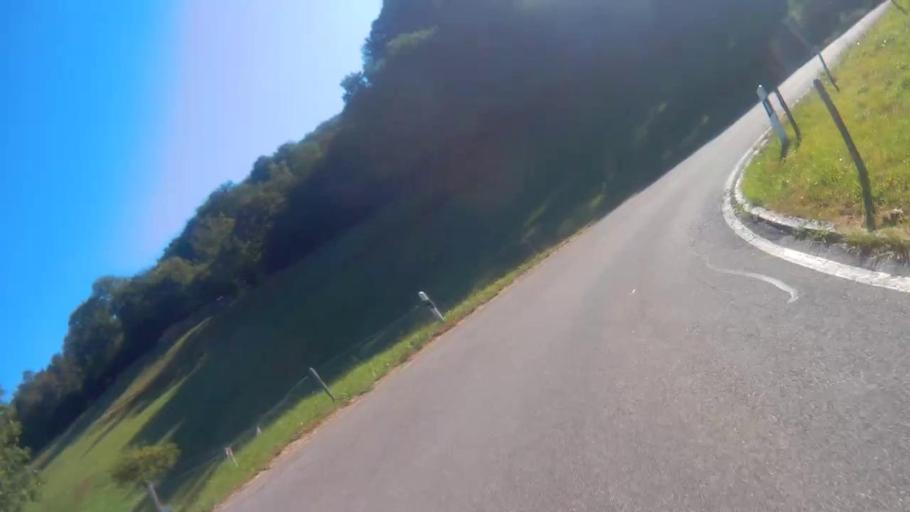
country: DE
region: Baden-Wuerttemberg
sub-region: Freiburg Region
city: Wembach
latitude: 47.7667
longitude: 7.8915
